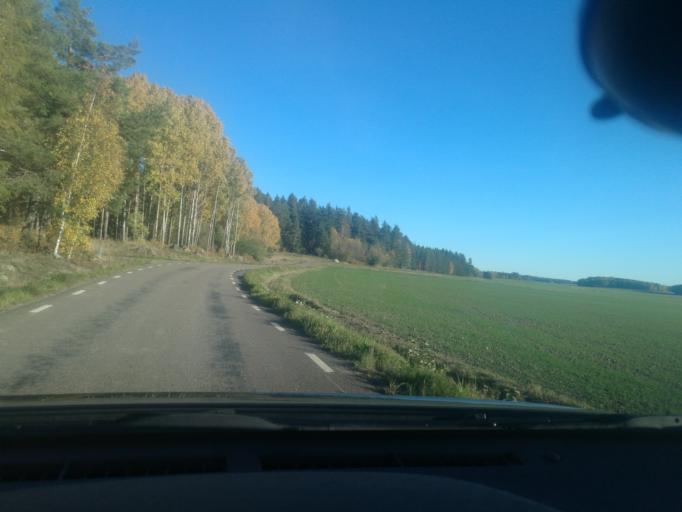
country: SE
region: Vaestmanland
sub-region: Kopings Kommun
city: Koping
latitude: 59.5752
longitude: 16.0122
